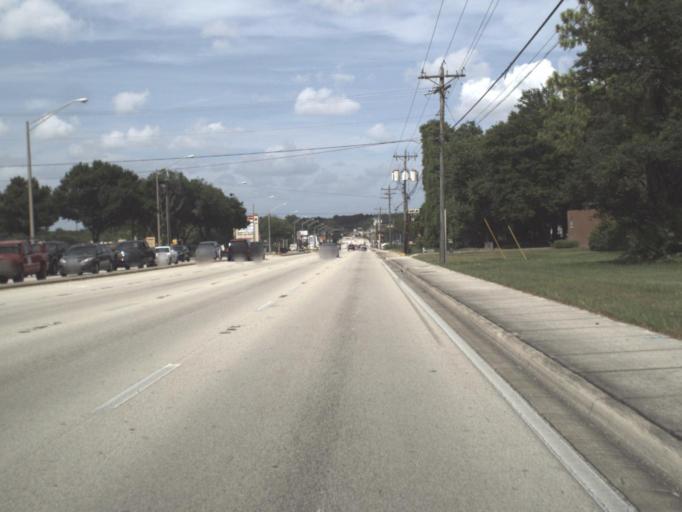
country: US
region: Florida
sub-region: Clay County
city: Lakeside
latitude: 30.1463
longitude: -81.7598
